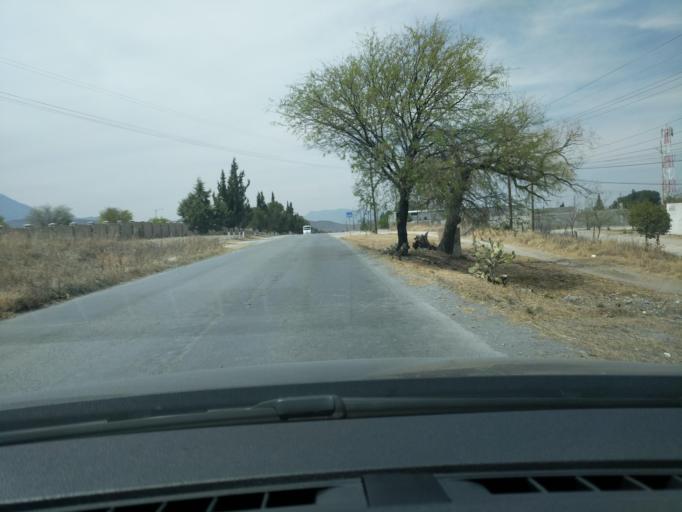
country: MX
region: Coahuila
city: Saltillo
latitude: 25.3544
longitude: -101.0277
